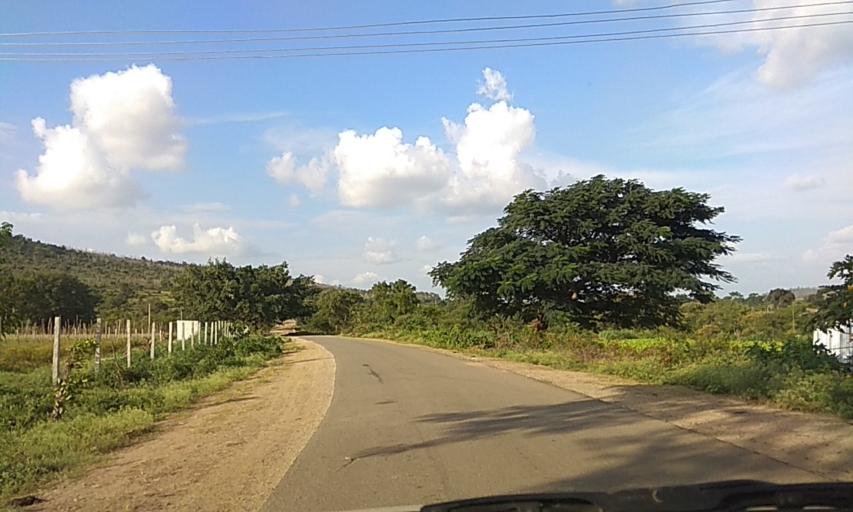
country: IN
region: Karnataka
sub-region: Chamrajnagar
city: Gundlupet
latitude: 11.7757
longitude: 76.7872
